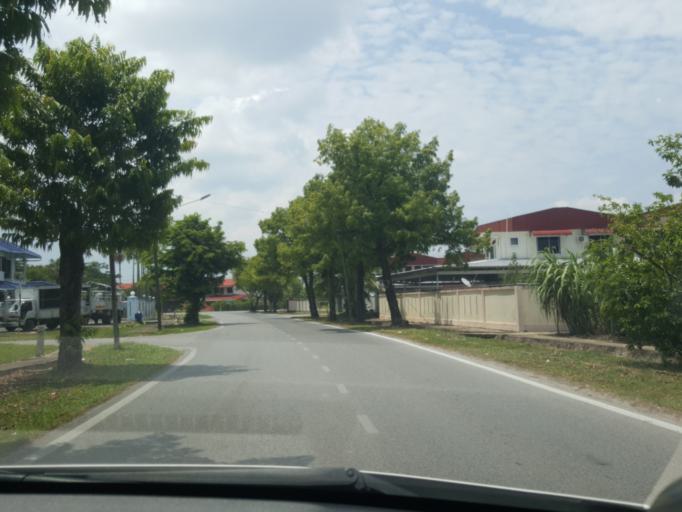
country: MY
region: Sarawak
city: Sarikei
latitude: 2.1238
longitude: 111.5242
